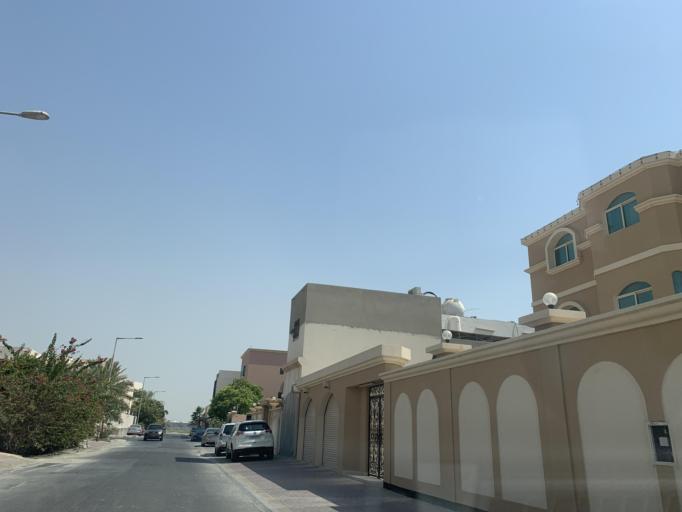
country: BH
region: Manama
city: Jidd Hafs
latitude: 26.2008
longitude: 50.5282
